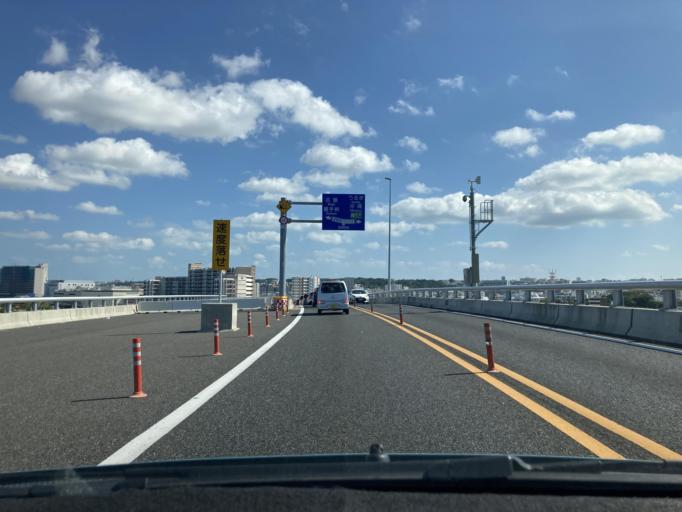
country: JP
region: Okinawa
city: Ginowan
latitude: 26.2726
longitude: 127.7231
